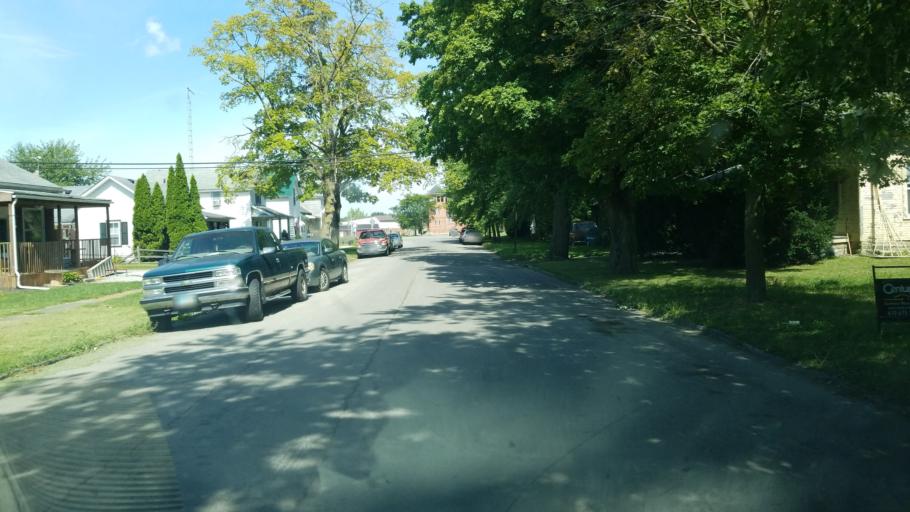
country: US
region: Ohio
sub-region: Hardin County
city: Kenton
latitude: 40.6394
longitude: -83.6079
